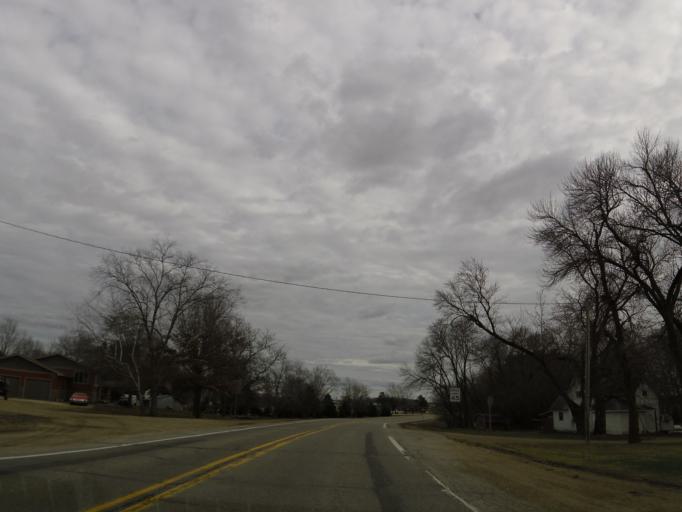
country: US
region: Minnesota
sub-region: Fillmore County
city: Spring Valley
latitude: 43.4894
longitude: -92.3565
